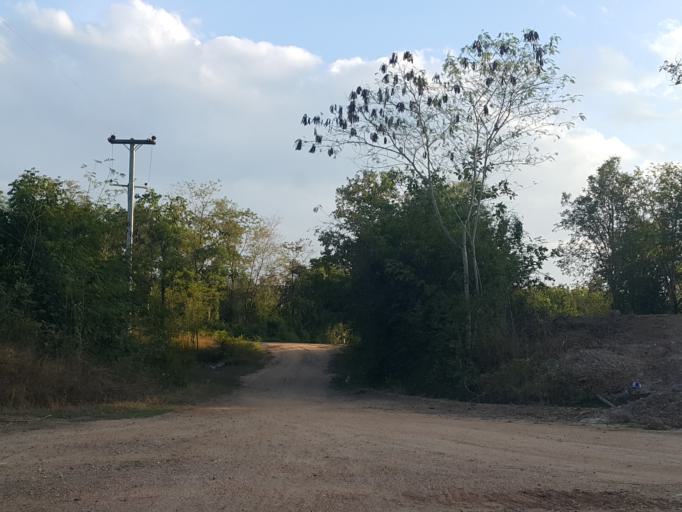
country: TH
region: Lampang
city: Lampang
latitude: 18.4340
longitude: 99.5822
